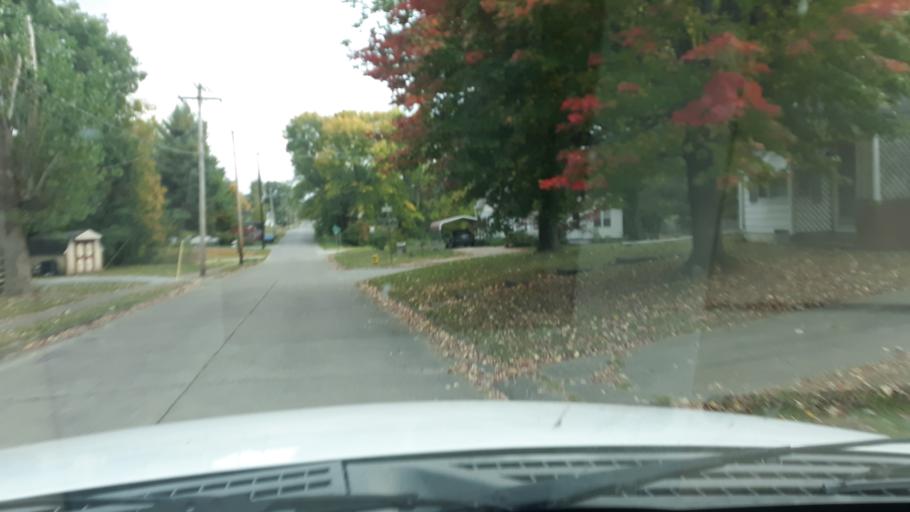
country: US
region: Illinois
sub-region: Saline County
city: Eldorado
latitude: 37.8156
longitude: -88.4337
